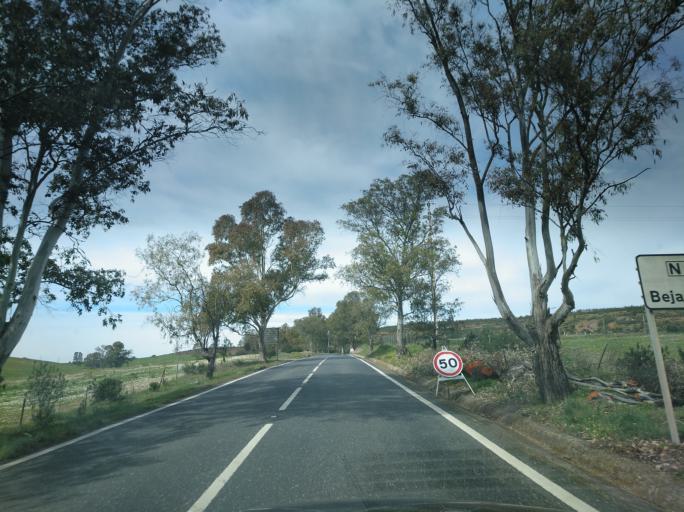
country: PT
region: Beja
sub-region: Mertola
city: Mertola
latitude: 37.7040
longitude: -7.7489
